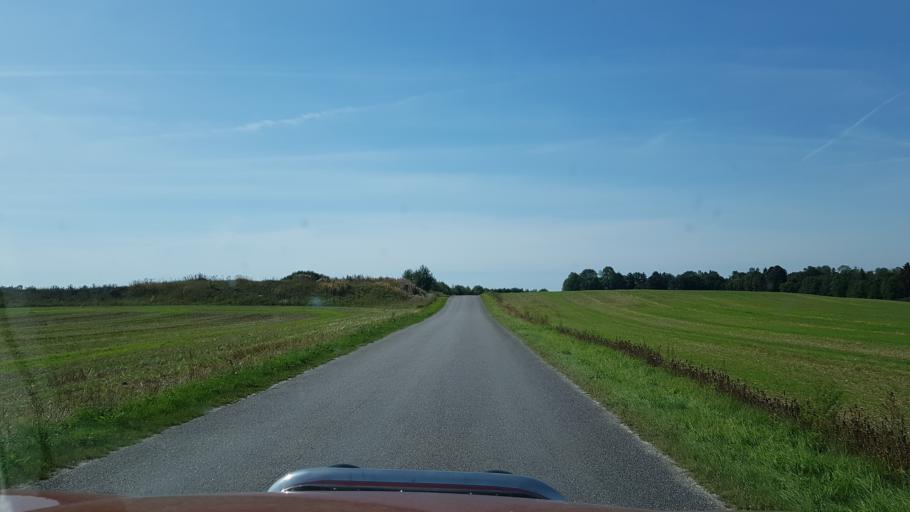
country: EE
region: Viljandimaa
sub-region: Vohma linn
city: Vohma
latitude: 58.5220
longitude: 25.6526
